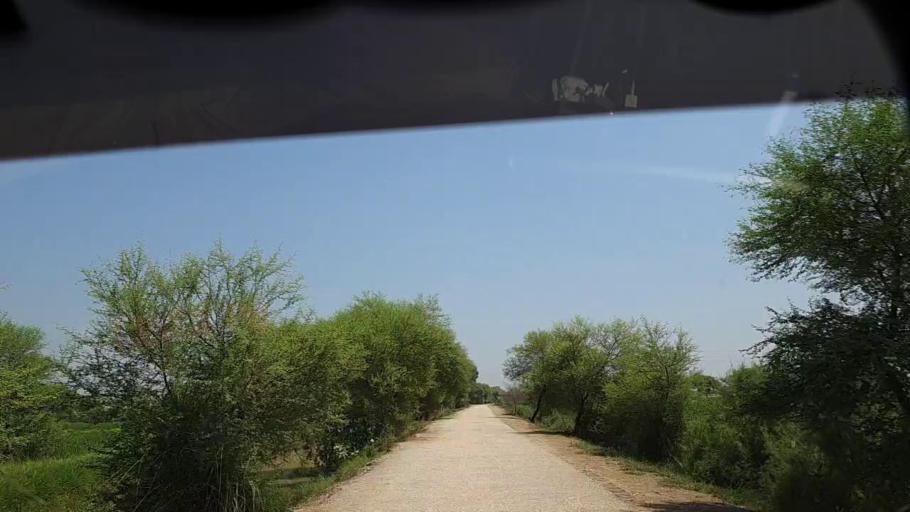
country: PK
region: Sindh
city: Ghauspur
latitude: 28.1704
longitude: 69.0648
